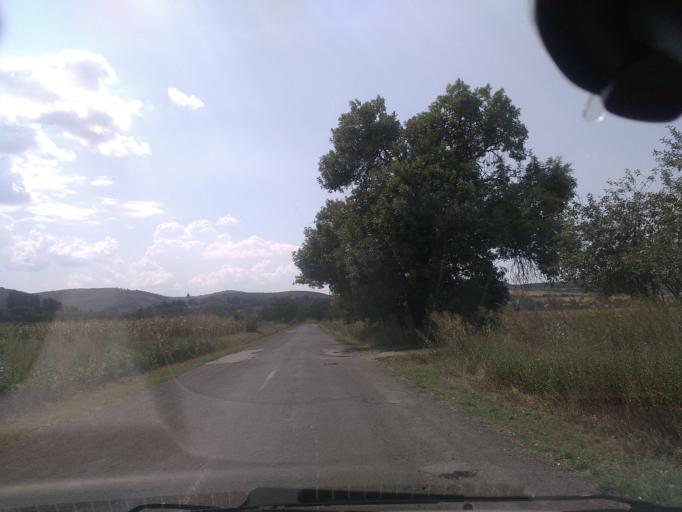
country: HU
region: Komarom-Esztergom
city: Pilismarot
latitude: 47.7919
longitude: 18.8795
